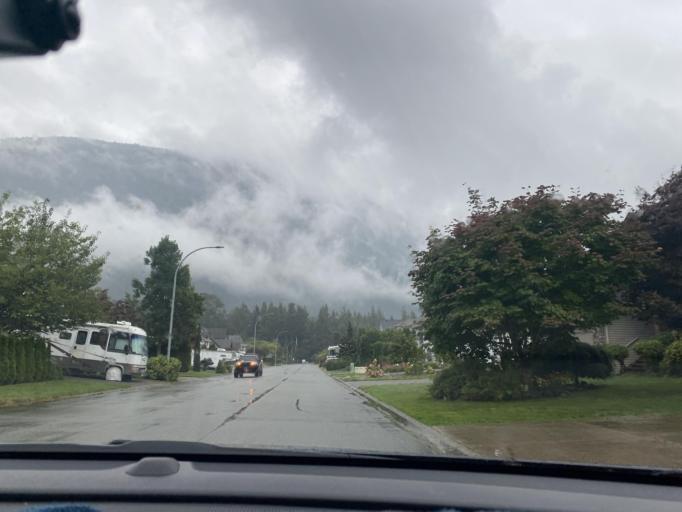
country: CA
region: British Columbia
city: Agassiz
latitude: 49.2955
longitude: -121.7816
